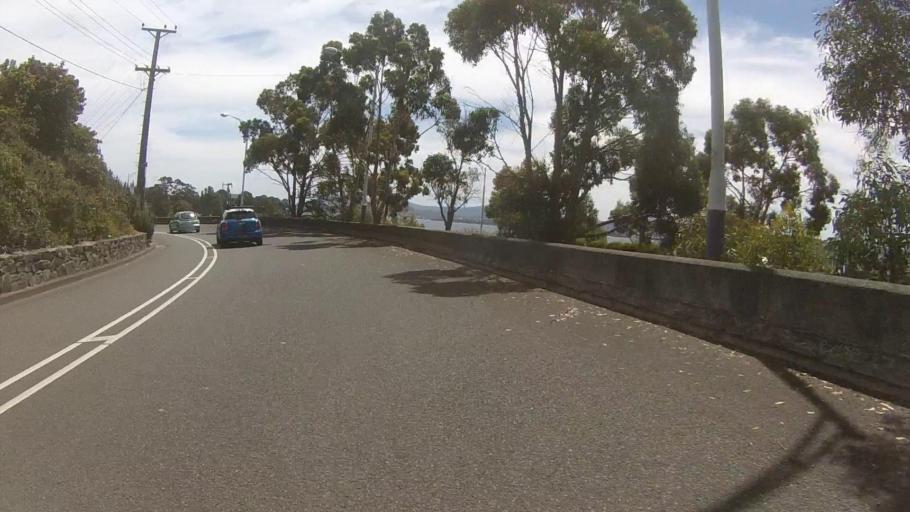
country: AU
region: Tasmania
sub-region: Kingborough
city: Taroona
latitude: -42.9147
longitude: 147.3591
